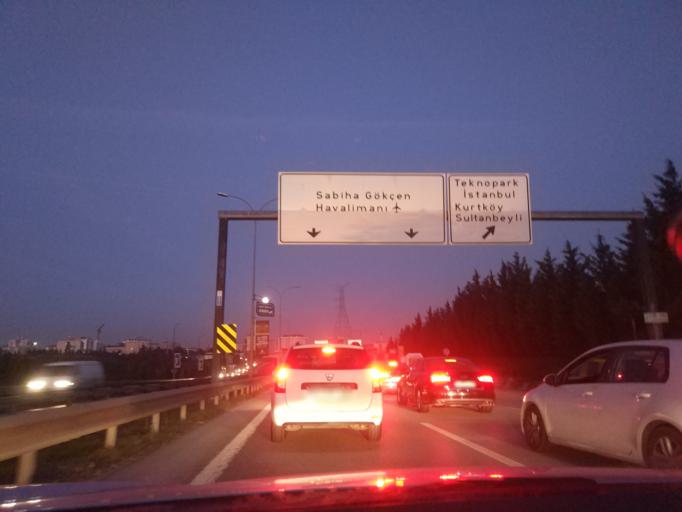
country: TR
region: Istanbul
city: Pendik
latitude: 40.9145
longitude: 29.3161
